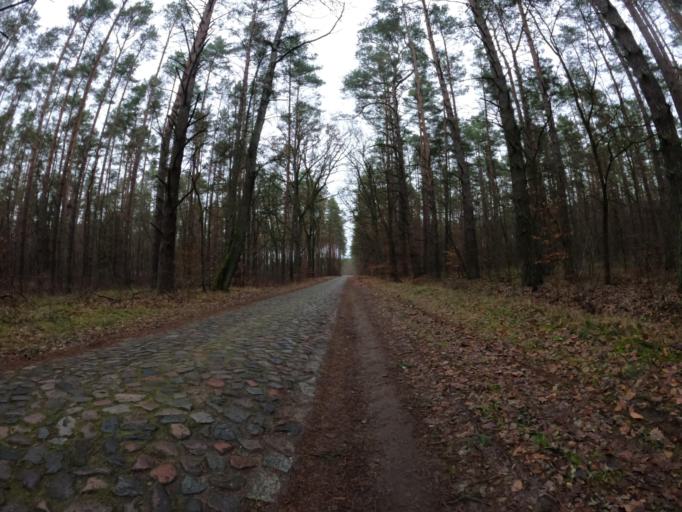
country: PL
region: West Pomeranian Voivodeship
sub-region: Powiat mysliborski
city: Debno
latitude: 52.7104
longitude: 14.7216
